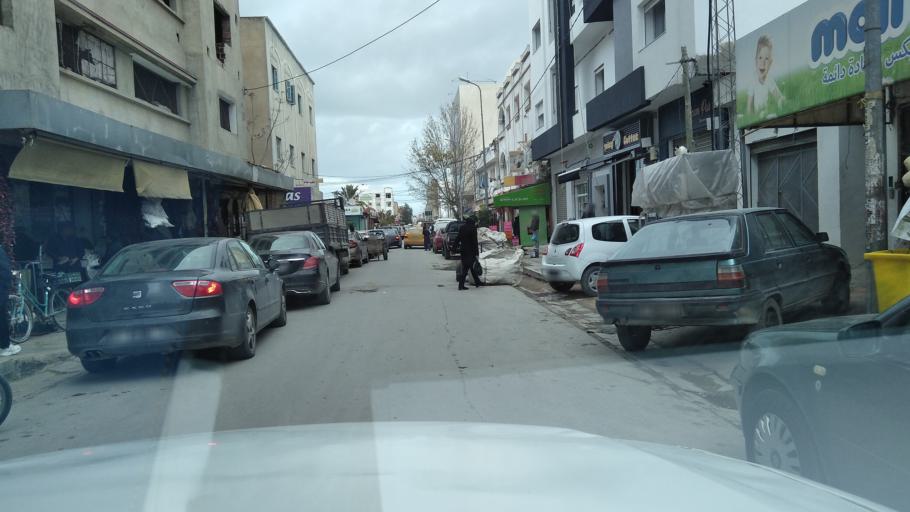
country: TN
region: Bin 'Arus
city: Ben Arous
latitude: 36.7556
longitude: 10.2212
